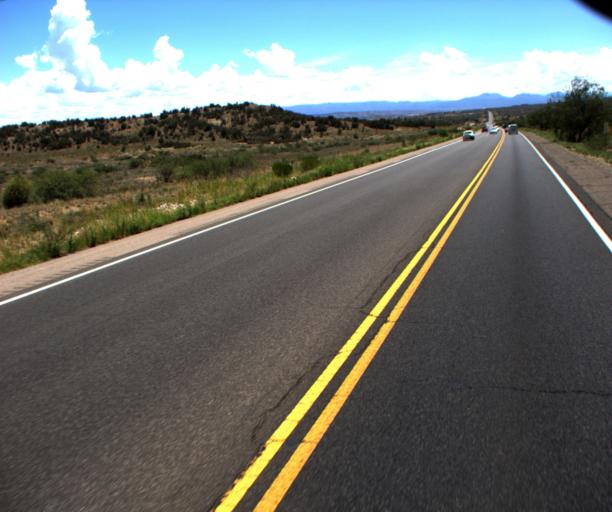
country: US
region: Arizona
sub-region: Yavapai County
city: Cornville
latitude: 34.6477
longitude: -111.9541
